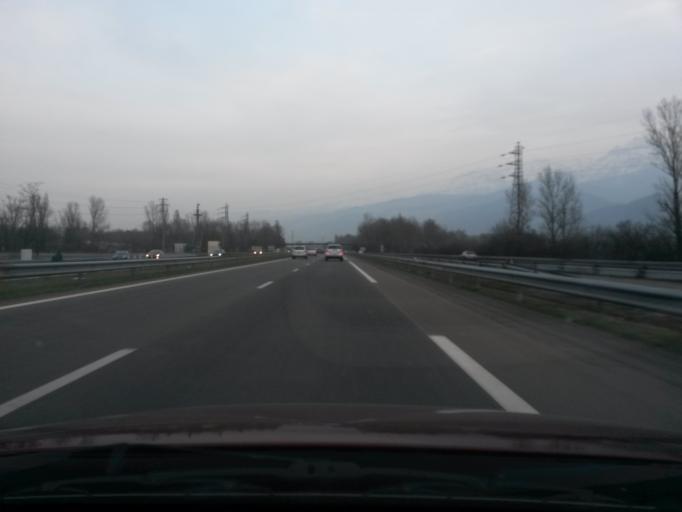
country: FR
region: Rhone-Alpes
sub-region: Departement de l'Isere
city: Corenc
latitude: 45.2045
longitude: 5.7840
